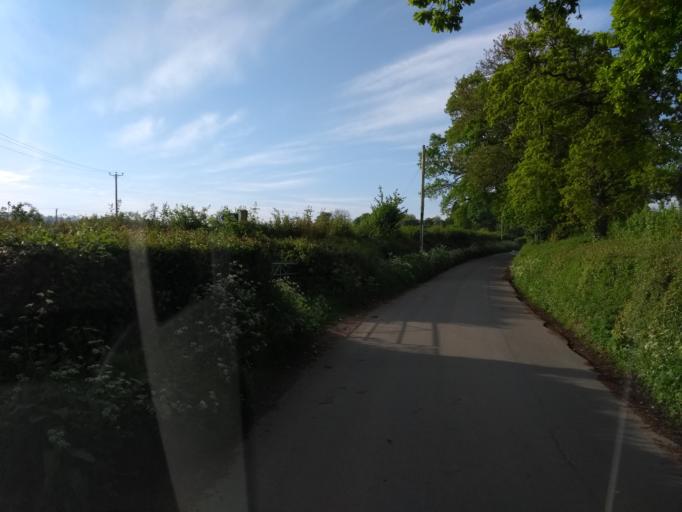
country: GB
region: England
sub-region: Devon
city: Axminster
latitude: 50.8091
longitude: -2.9516
